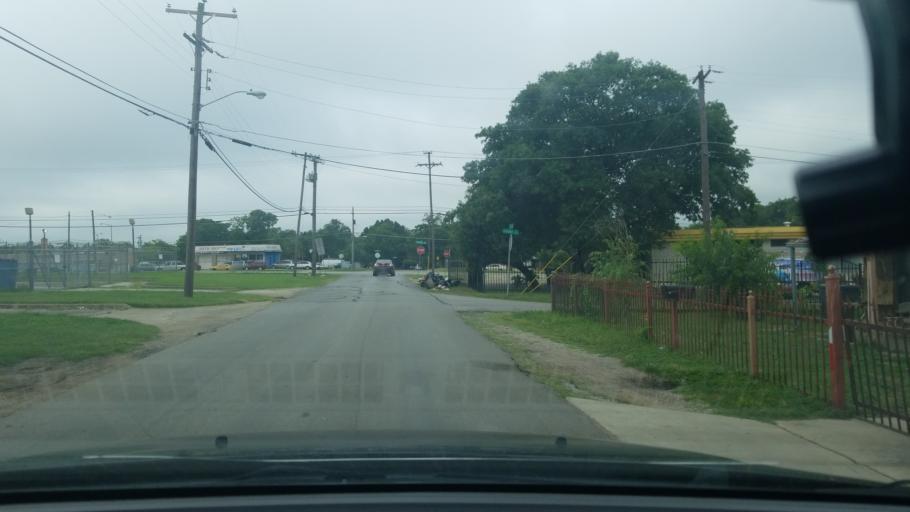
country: US
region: Texas
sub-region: Dallas County
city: Balch Springs
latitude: 32.7721
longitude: -96.6919
